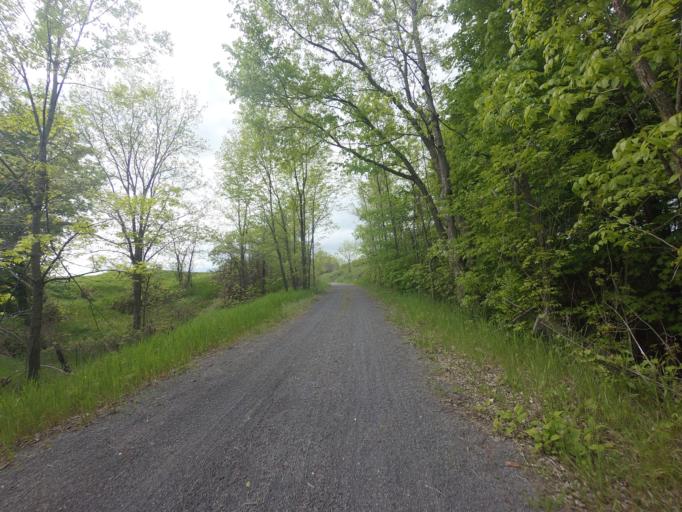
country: CA
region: Ontario
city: Kingston
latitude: 44.4013
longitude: -76.6420
